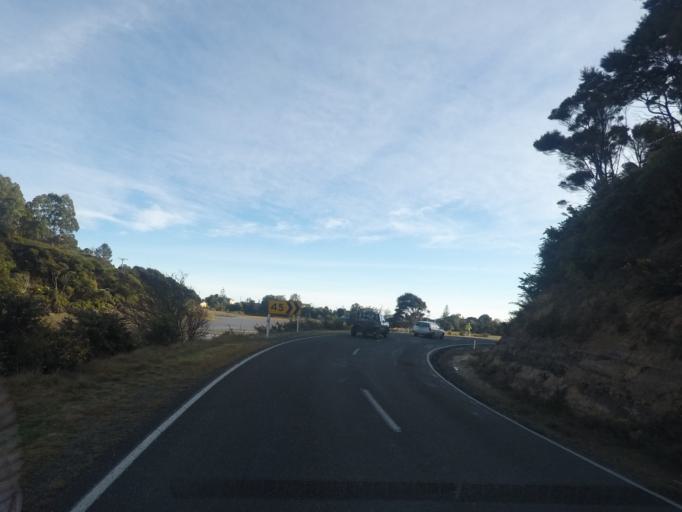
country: NZ
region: Tasman
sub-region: Tasman District
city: Takaka
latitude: -40.8168
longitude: 172.9148
